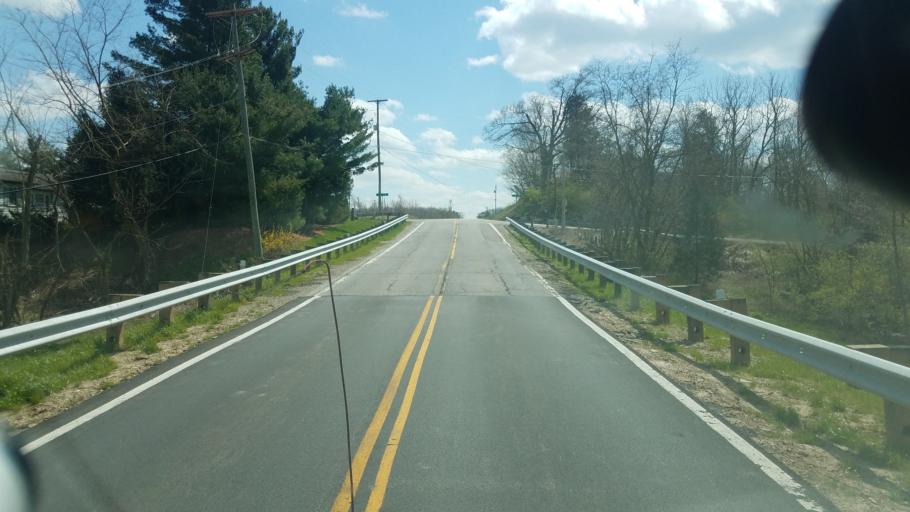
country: US
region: Ohio
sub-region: Licking County
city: Johnstown
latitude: 40.0967
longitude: -82.6623
